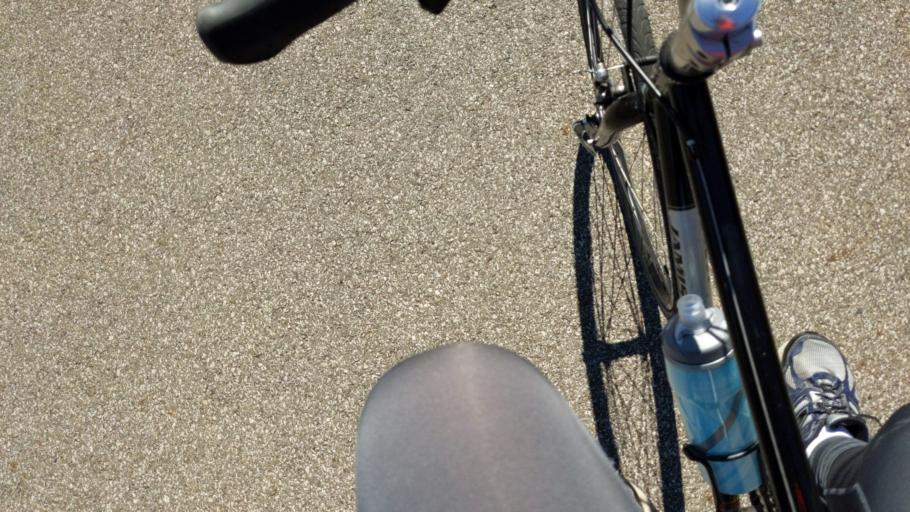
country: US
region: Ohio
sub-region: Cuyahoga County
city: Cleveland
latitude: 41.4721
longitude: -81.6882
